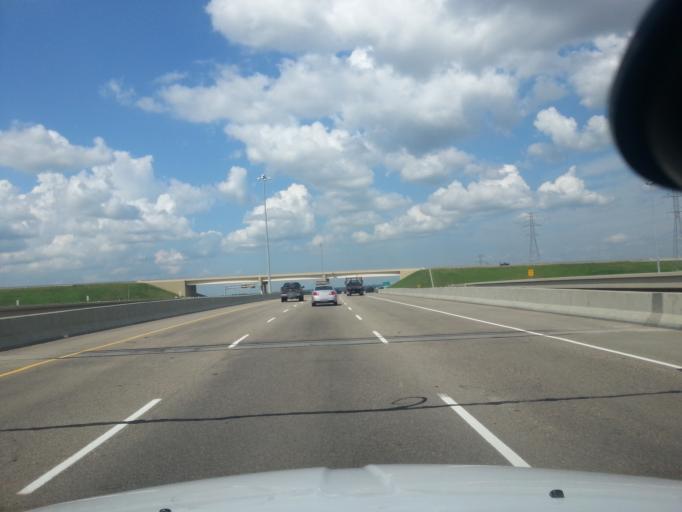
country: CA
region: Alberta
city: St. Albert
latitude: 53.5732
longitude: -113.6614
